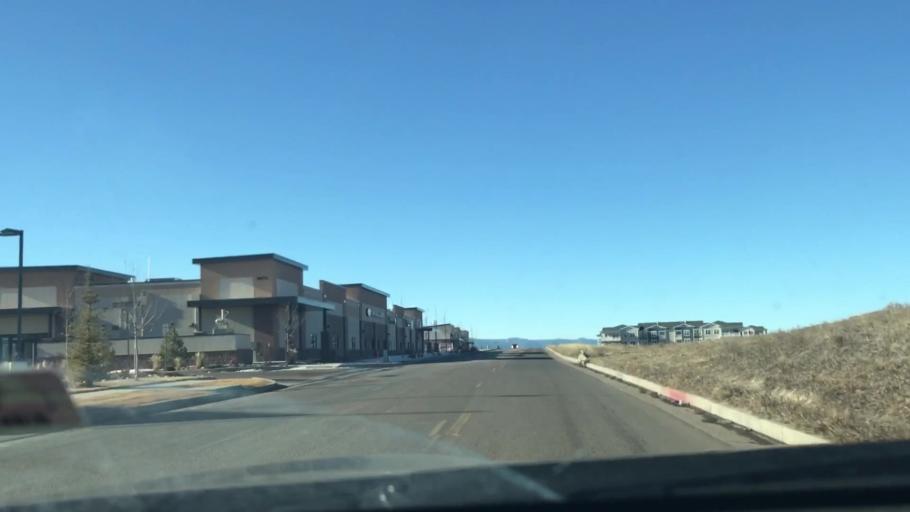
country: US
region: Colorado
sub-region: El Paso County
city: Black Forest
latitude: 38.9709
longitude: -104.7412
